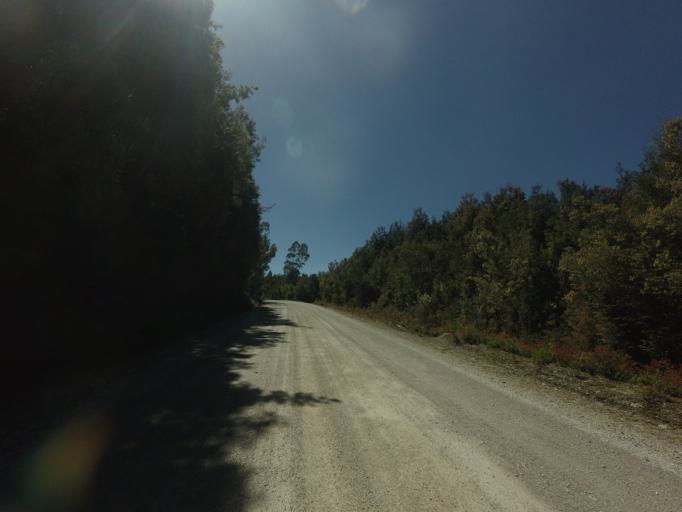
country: AU
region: Tasmania
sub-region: Huon Valley
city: Geeveston
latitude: -42.8328
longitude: 146.3844
